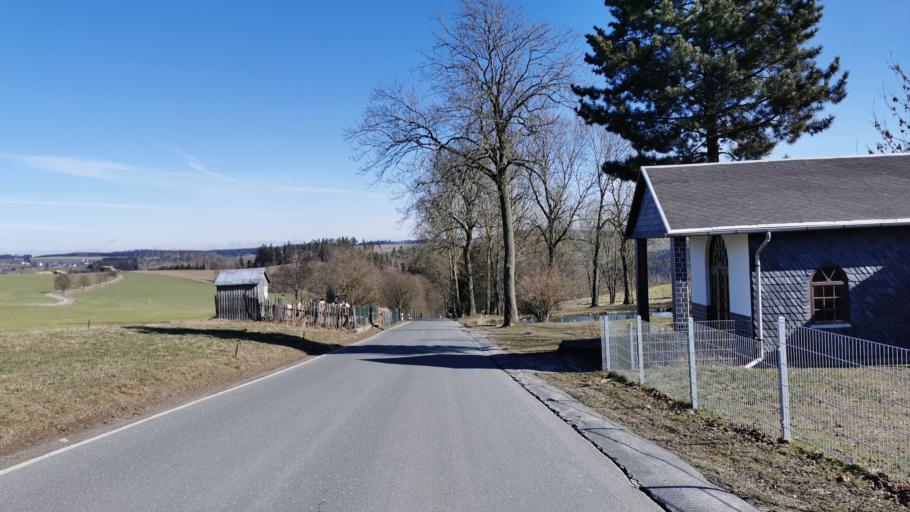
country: DE
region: Thuringia
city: Wurzbach
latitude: 50.5069
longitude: 11.5014
